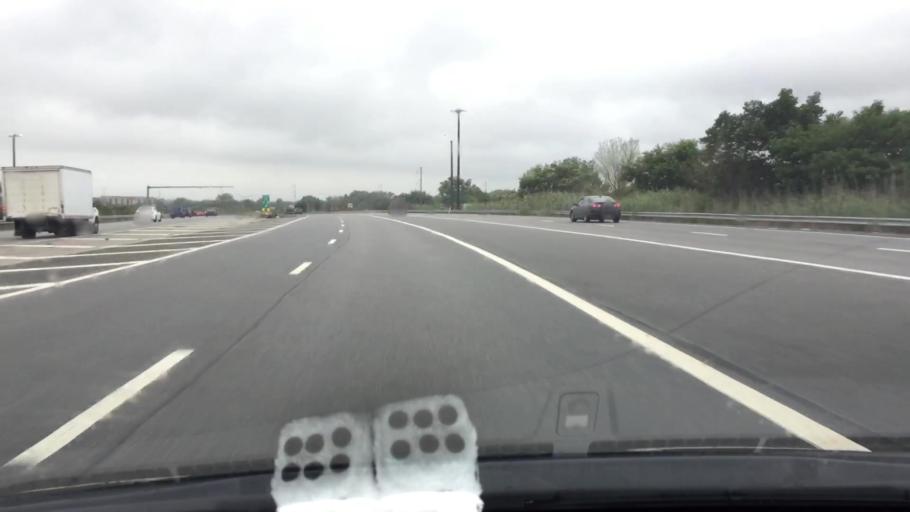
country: US
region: Pennsylvania
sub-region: Delaware County
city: Colwyn
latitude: 39.8938
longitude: -75.2335
